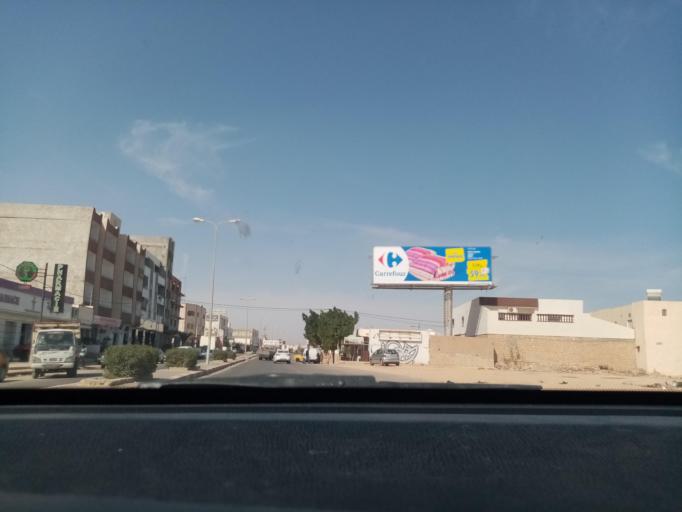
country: TN
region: Qabis
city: Gabes
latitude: 33.8495
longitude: 10.1118
